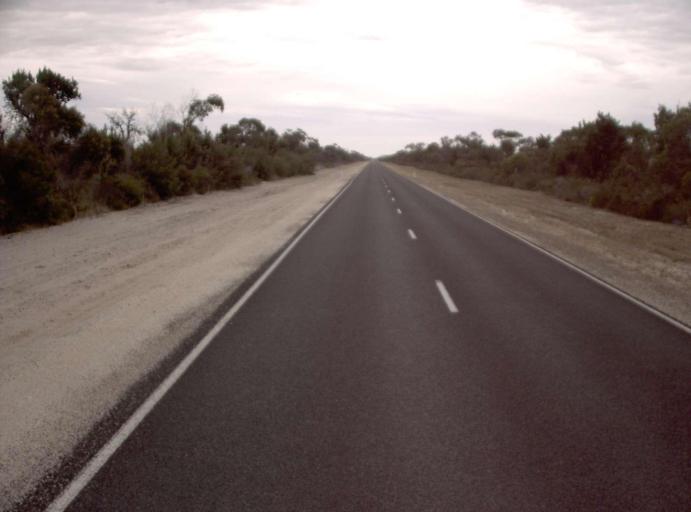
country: AU
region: Victoria
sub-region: East Gippsland
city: Bairnsdale
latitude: -38.1235
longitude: 147.4514
